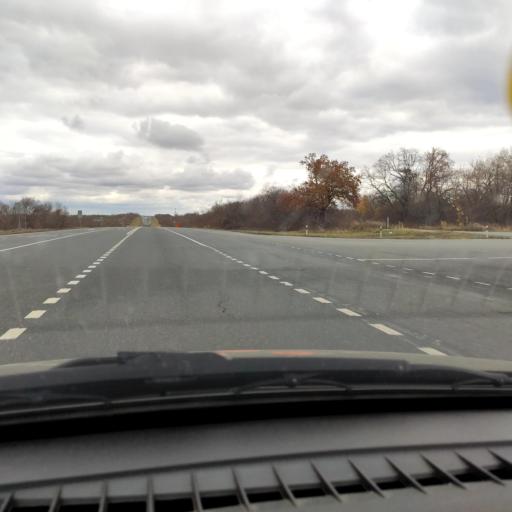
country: RU
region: Samara
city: Mezhdurechensk
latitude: 53.2580
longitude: 49.1046
